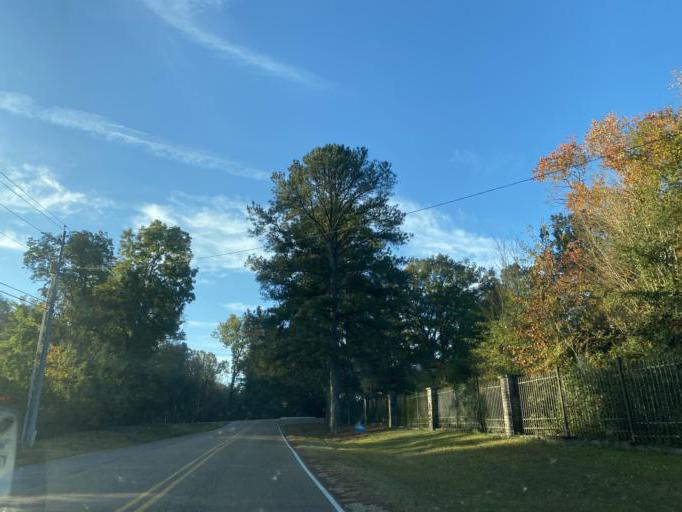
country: US
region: Mississippi
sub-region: Madison County
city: Madison
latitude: 32.4660
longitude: -90.0721
